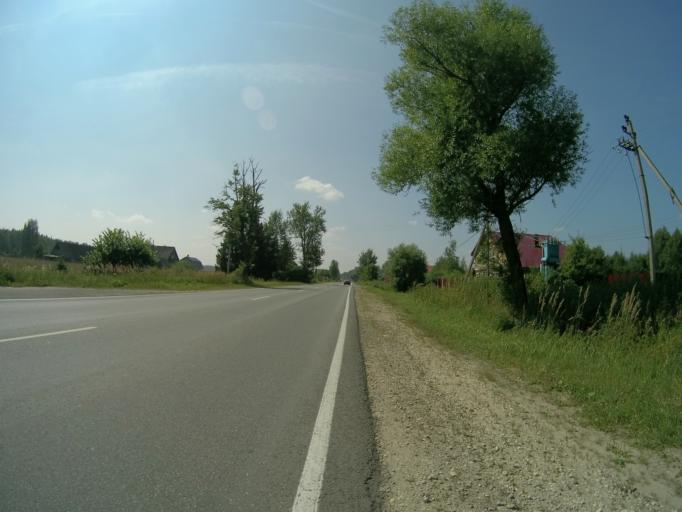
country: RU
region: Vladimir
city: Anopino
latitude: 55.6907
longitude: 40.7468
